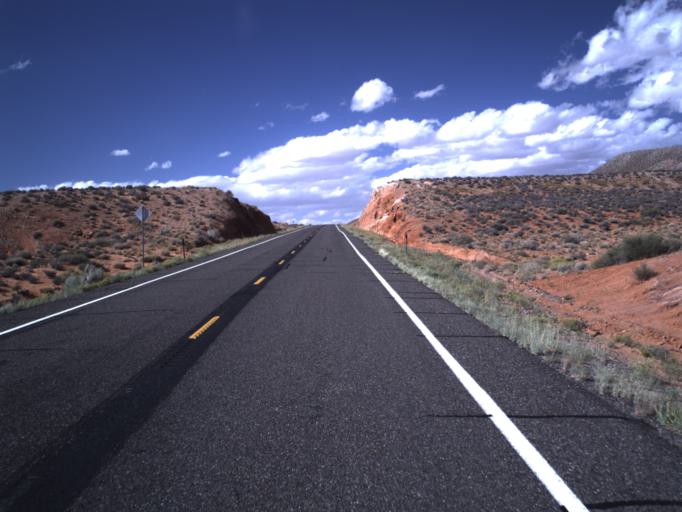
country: US
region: Utah
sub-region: Wayne County
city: Loa
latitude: 38.0727
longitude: -110.6079
